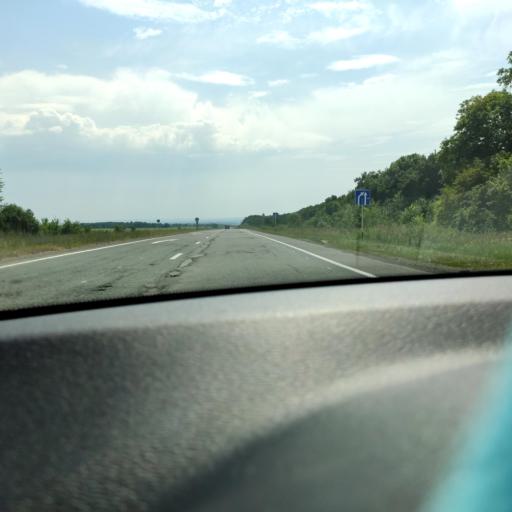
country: RU
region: Samara
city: Petra-Dubrava
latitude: 53.3321
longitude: 50.4288
